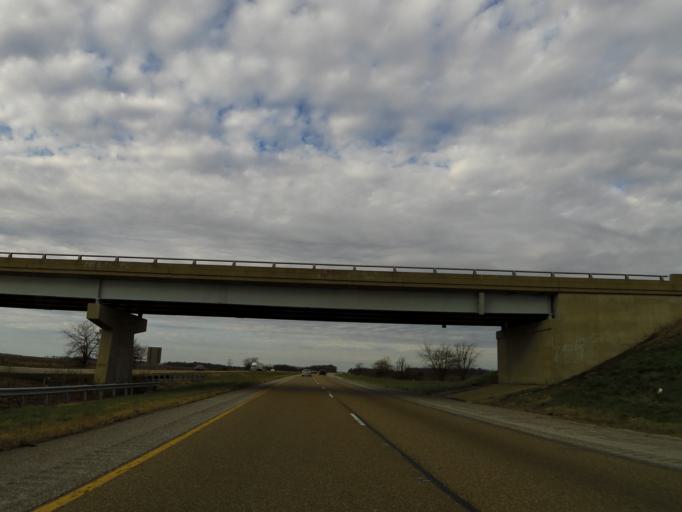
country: US
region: Illinois
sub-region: Clinton County
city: Wamac
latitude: 38.3889
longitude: -89.1910
